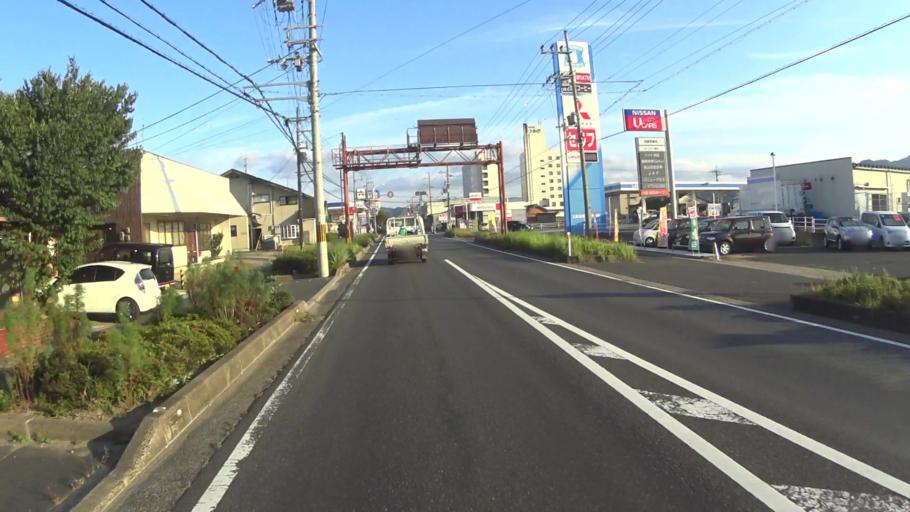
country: JP
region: Kyoto
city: Miyazu
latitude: 35.6078
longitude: 135.0811
